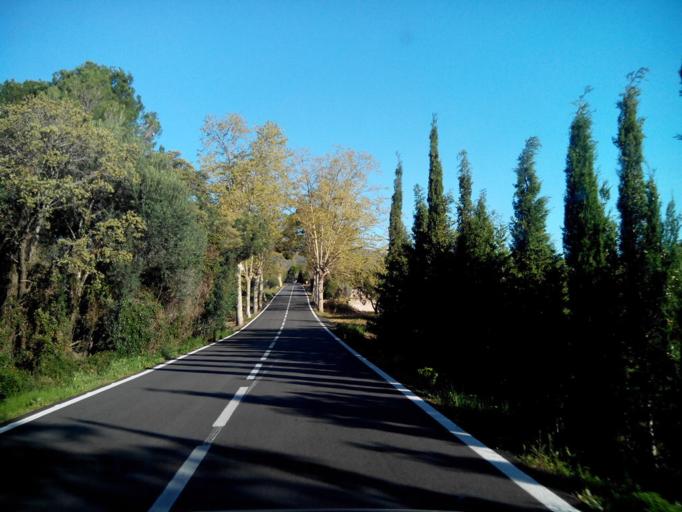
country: ES
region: Catalonia
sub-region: Provincia de Tarragona
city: Riudecanyes
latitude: 41.1010
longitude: 0.9647
